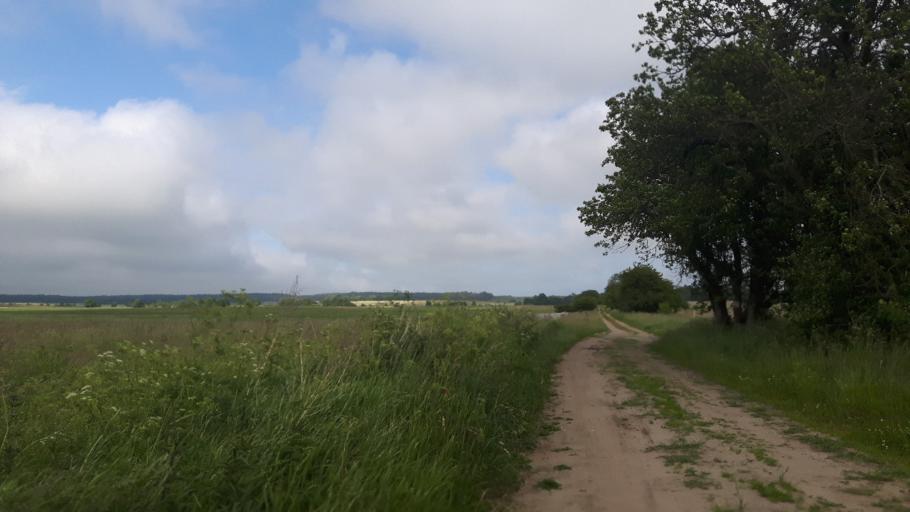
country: PL
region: Pomeranian Voivodeship
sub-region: Powiat slupski
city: Ustka
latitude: 54.5932
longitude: 16.9748
